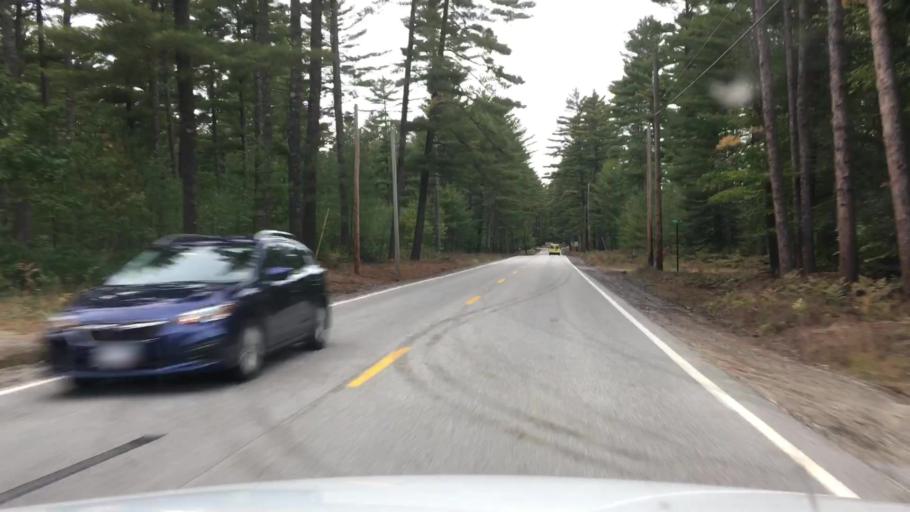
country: US
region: Maine
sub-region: Cumberland County
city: Harrison
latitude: 44.2269
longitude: -70.7013
